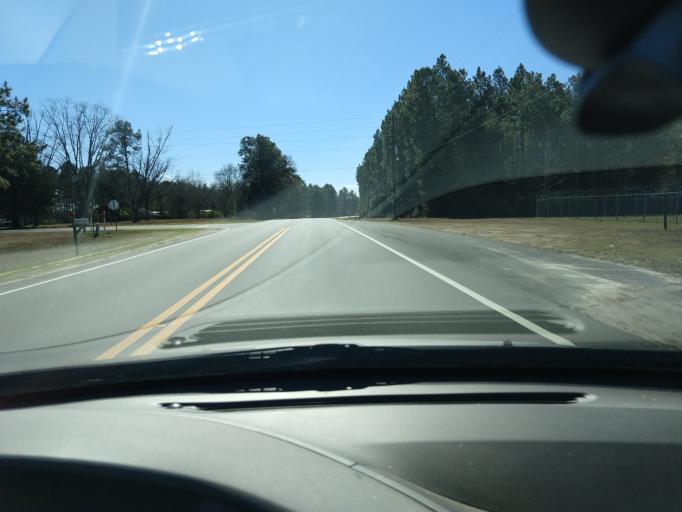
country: US
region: Alabama
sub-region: Covington County
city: Andalusia
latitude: 31.2302
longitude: -86.5278
